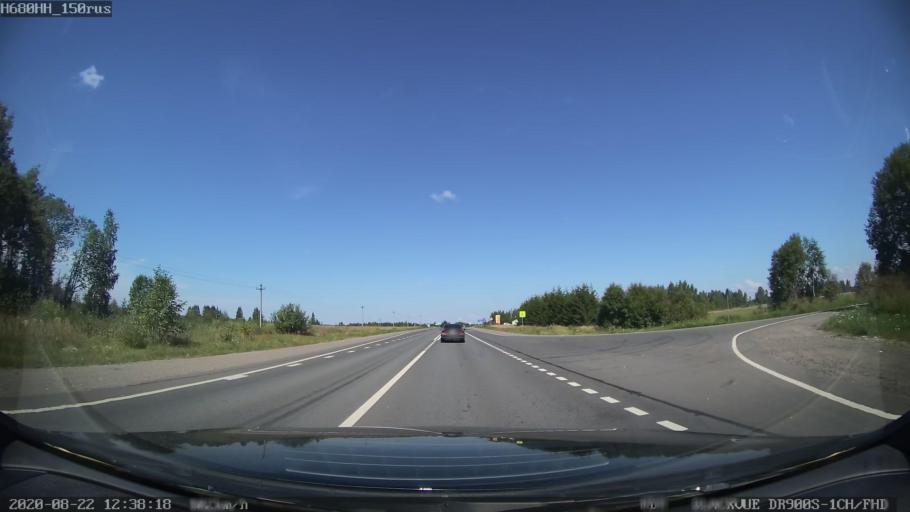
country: RU
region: Tverskaya
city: Rameshki
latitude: 57.3118
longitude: 36.0885
